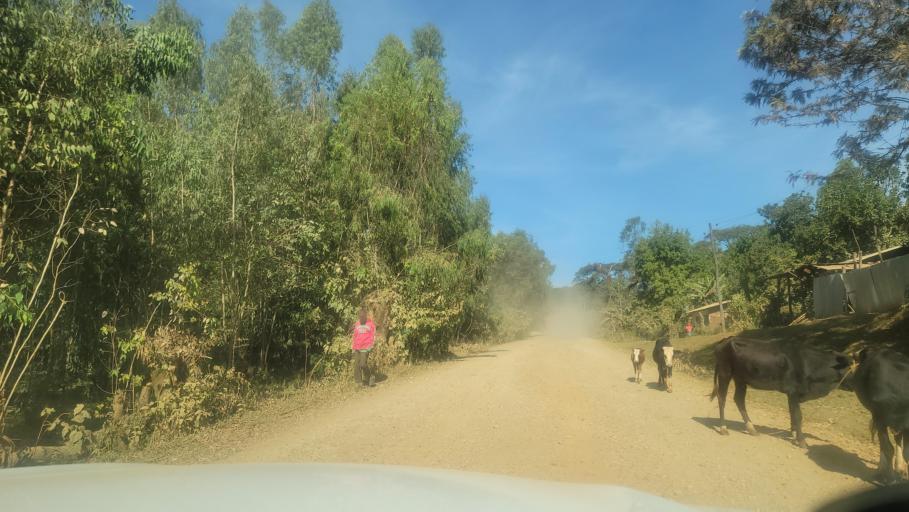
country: ET
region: Oromiya
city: Agaro
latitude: 7.8140
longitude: 36.5109
